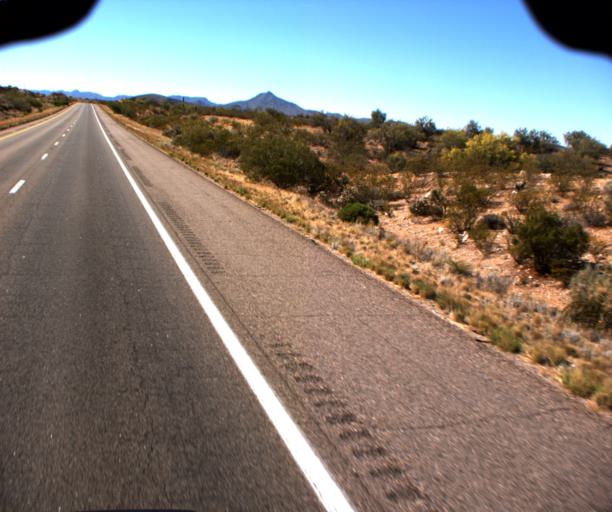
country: US
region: Arizona
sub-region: Yavapai County
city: Bagdad
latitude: 34.6059
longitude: -113.5224
